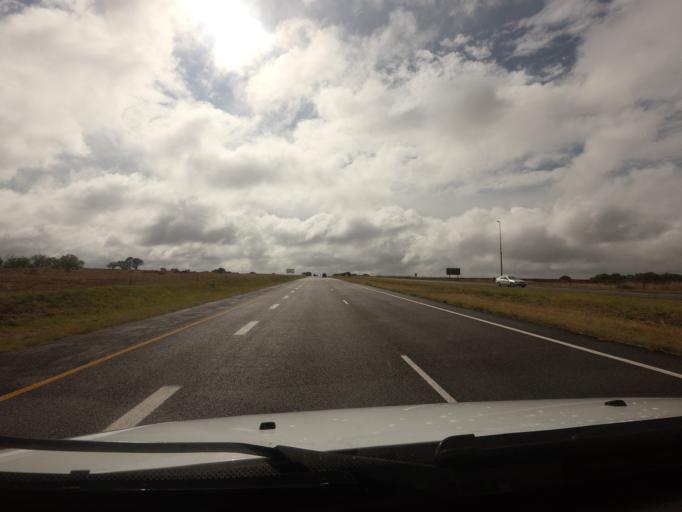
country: ZA
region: Gauteng
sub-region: City of Tshwane Metropolitan Municipality
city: Bronkhorstspruit
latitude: -25.7991
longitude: 28.6229
